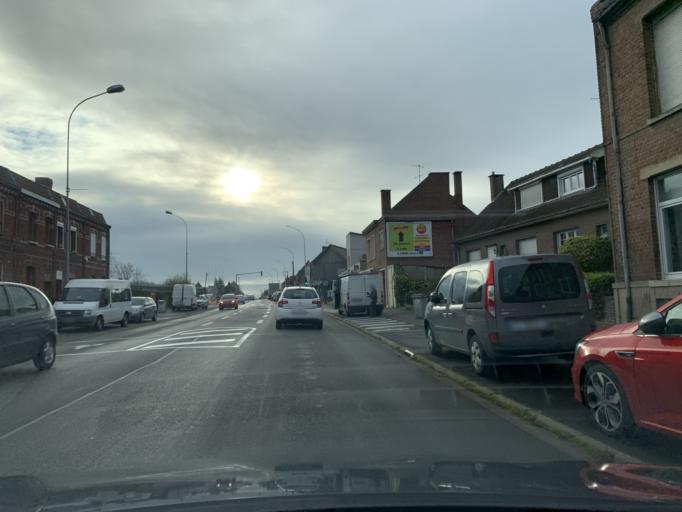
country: FR
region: Nord-Pas-de-Calais
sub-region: Departement du Nord
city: Lambres-lez-Douai
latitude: 50.3501
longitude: 3.0874
